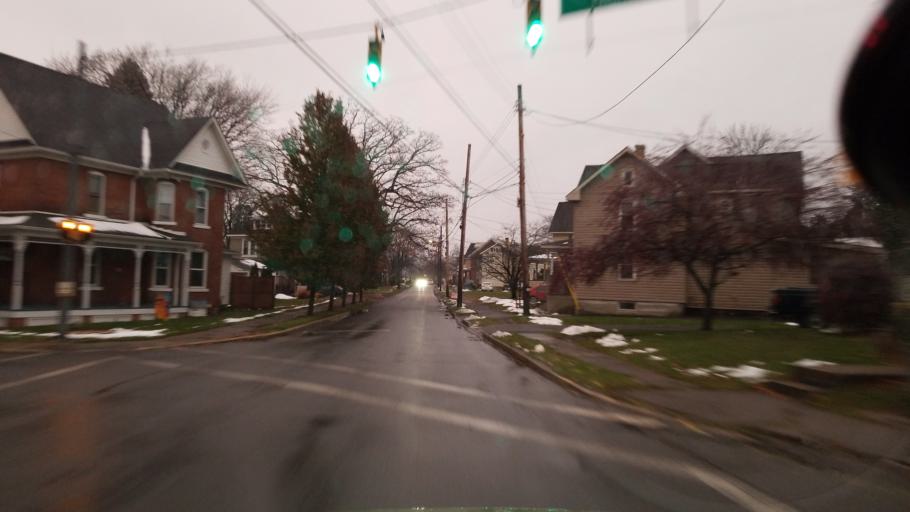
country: US
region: Pennsylvania
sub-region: Clearfield County
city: Clearfield
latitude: 41.0273
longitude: -78.4473
